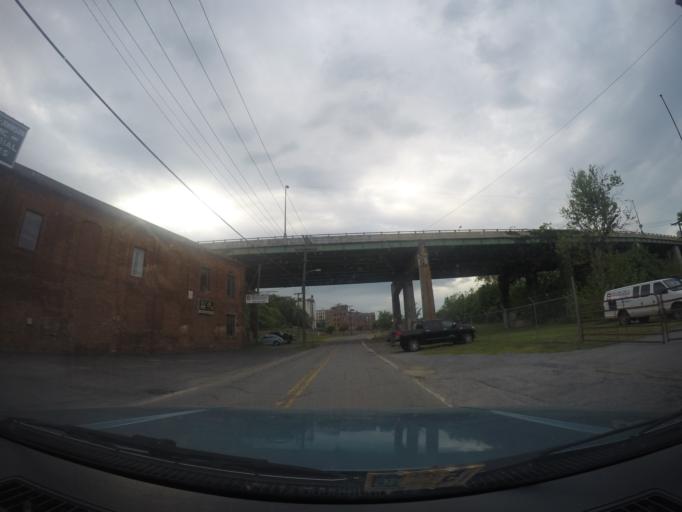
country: US
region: Virginia
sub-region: City of Lynchburg
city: Lynchburg
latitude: 37.4093
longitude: -79.1343
